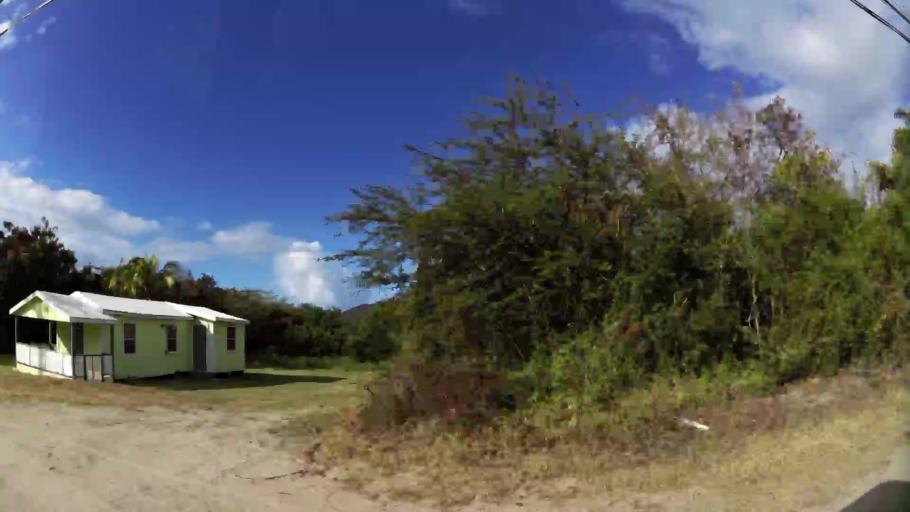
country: VG
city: Tortola
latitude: 18.4406
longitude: -64.4370
